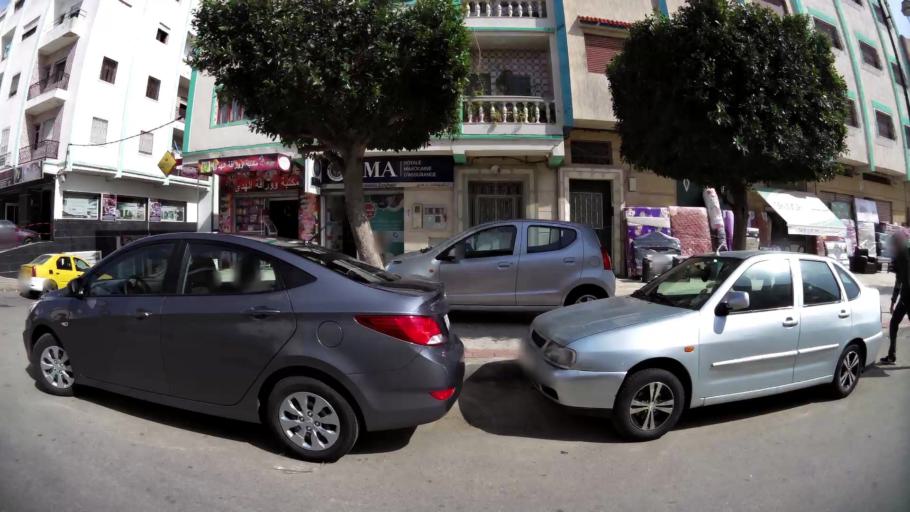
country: MA
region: Tanger-Tetouan
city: Tetouan
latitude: 35.5843
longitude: -5.3582
